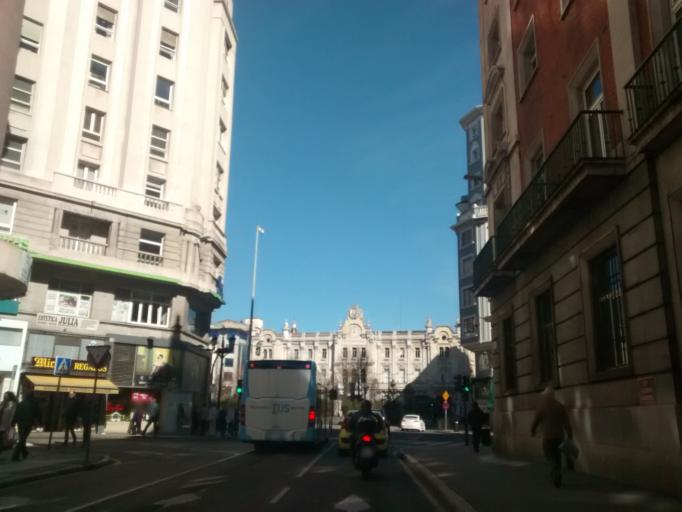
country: ES
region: Cantabria
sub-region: Provincia de Cantabria
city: Santander
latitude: 43.4610
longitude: -3.8094
